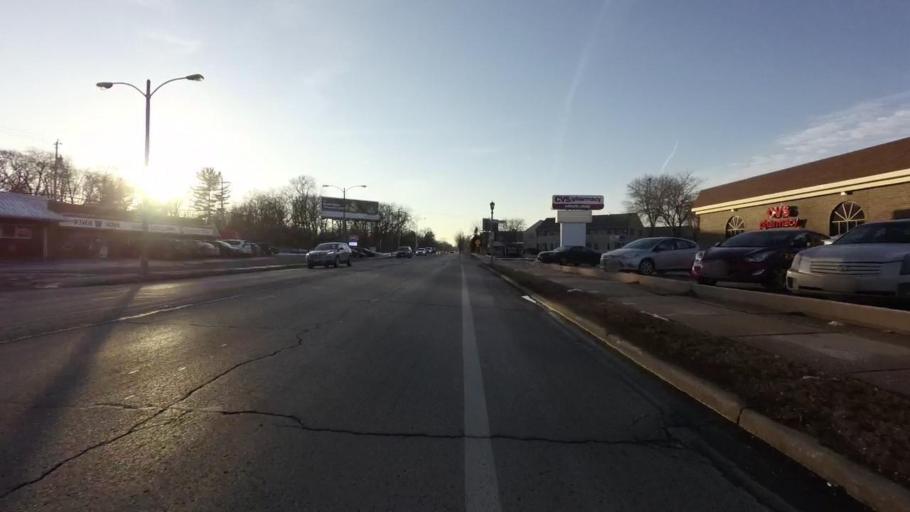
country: US
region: Wisconsin
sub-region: Milwaukee County
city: Whitefish Bay
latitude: 43.1040
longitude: -87.9067
